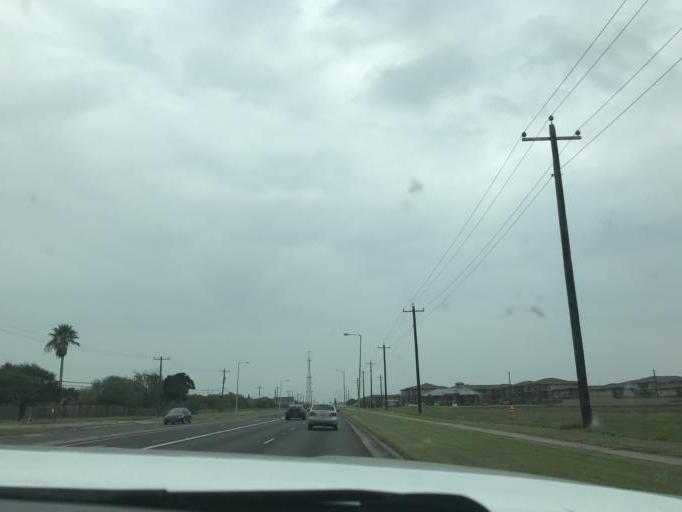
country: US
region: Texas
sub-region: Nueces County
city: Corpus Christi
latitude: 27.6747
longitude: -97.3623
